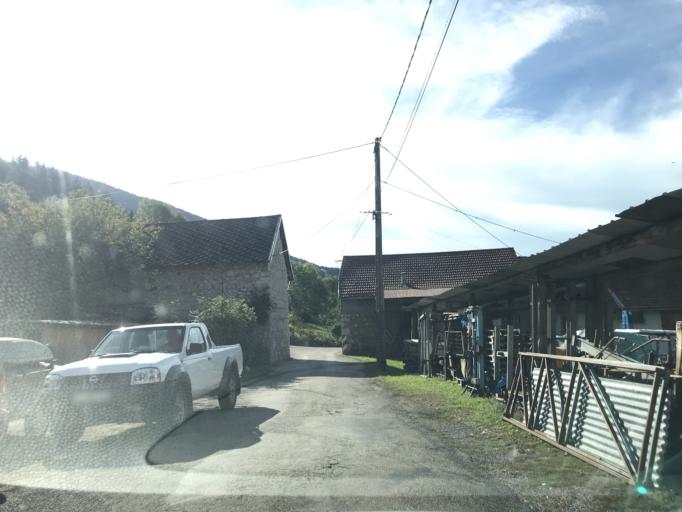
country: FR
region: Rhone-Alpes
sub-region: Departement de la Savoie
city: Novalaise
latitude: 45.6268
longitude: 5.8000
